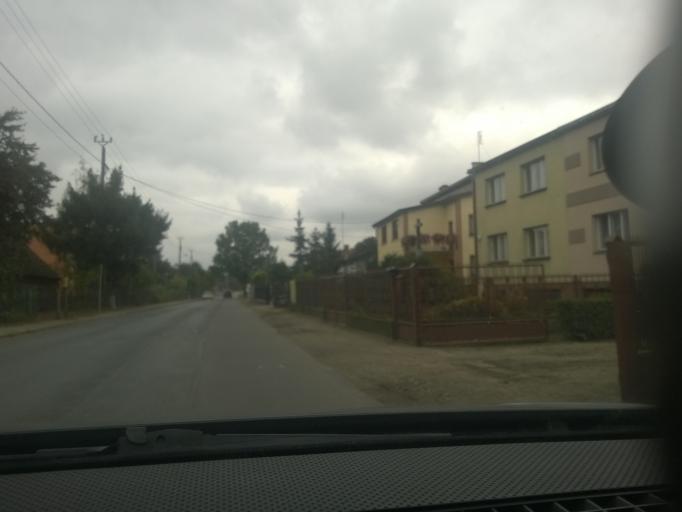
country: PL
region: Greater Poland Voivodeship
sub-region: Kalisz
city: Kalisz
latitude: 51.7265
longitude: 18.1350
